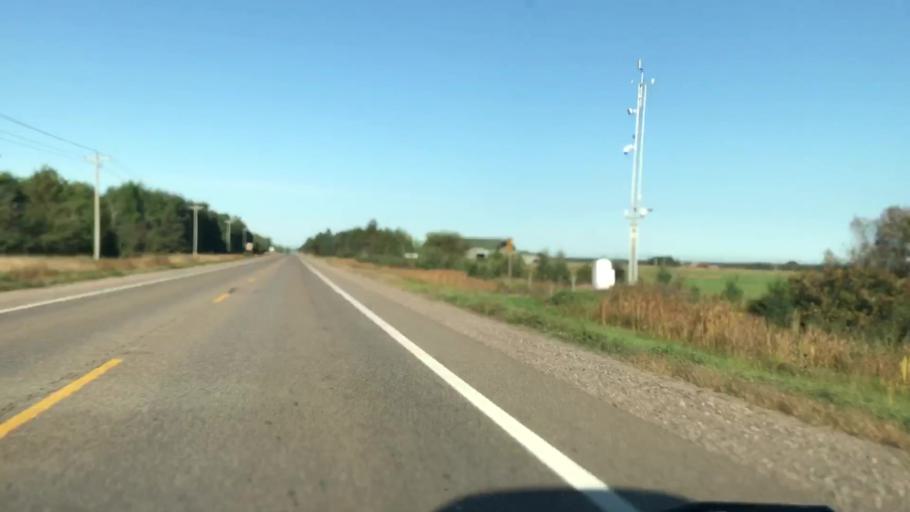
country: US
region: Michigan
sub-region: Chippewa County
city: Sault Ste. Marie
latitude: 46.3746
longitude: -84.4342
